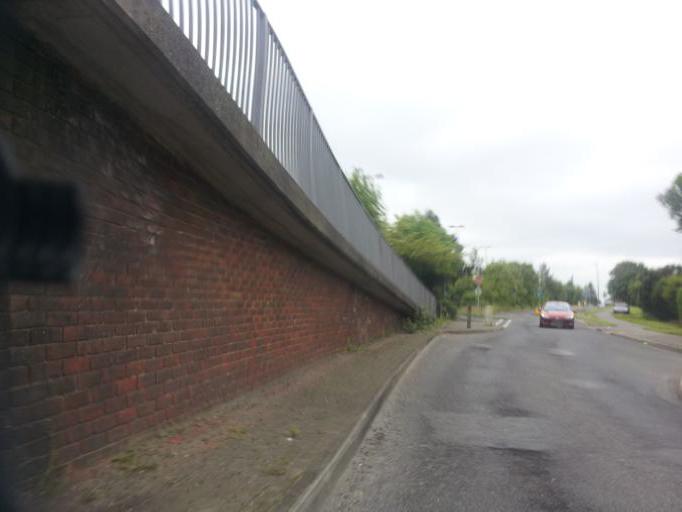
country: GB
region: England
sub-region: Kent
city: Maidstone
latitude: 51.2916
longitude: 0.5175
